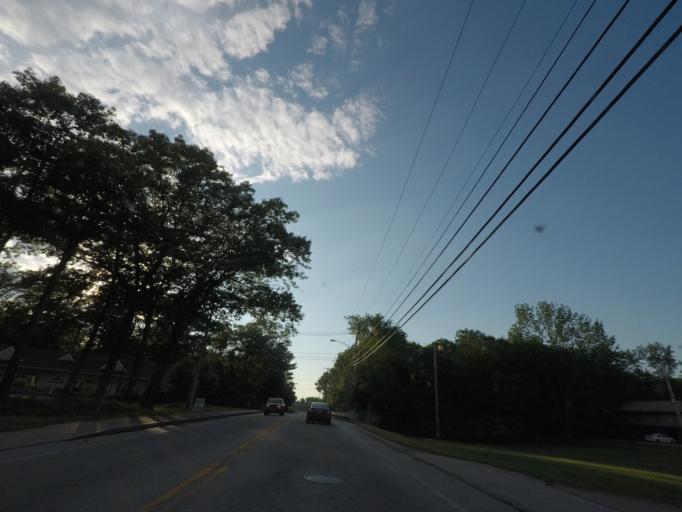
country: US
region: Massachusetts
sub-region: Worcester County
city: Sturbridge
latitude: 42.0939
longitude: -72.0690
